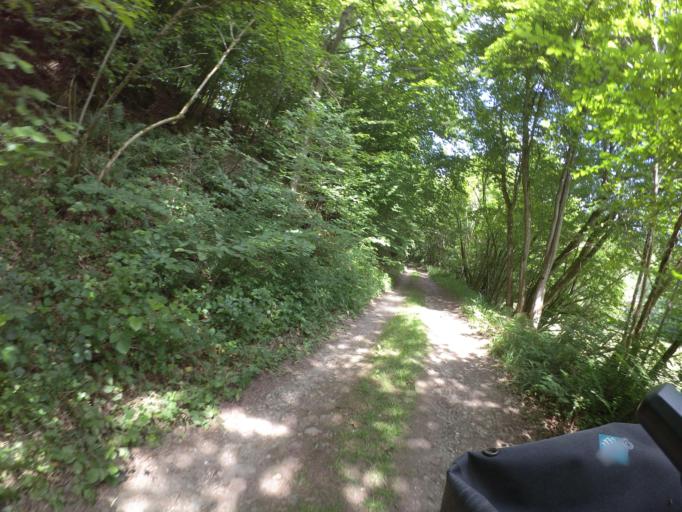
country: DE
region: Rheinland-Pfalz
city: Etgert
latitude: 49.7961
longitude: 7.0248
